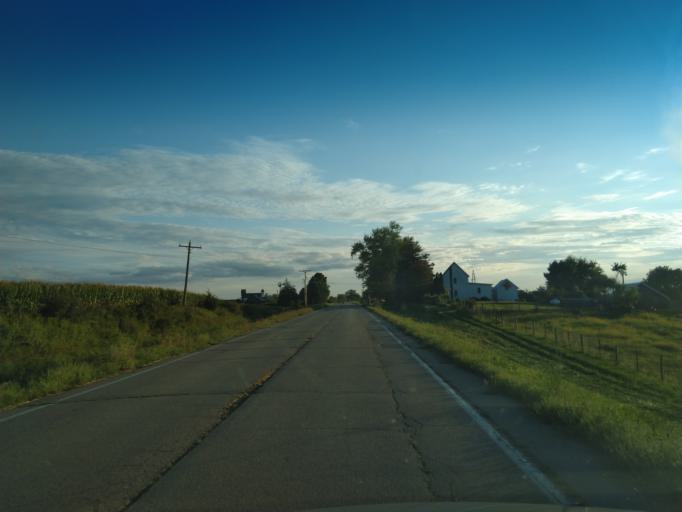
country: US
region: Iowa
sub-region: Jackson County
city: Maquoketa
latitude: 42.1491
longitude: -90.7578
